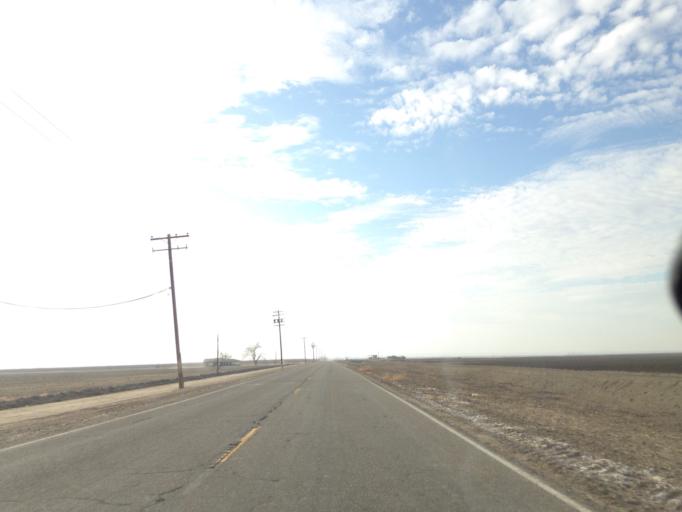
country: US
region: California
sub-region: Kern County
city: Buttonwillow
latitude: 35.4419
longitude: -119.5314
